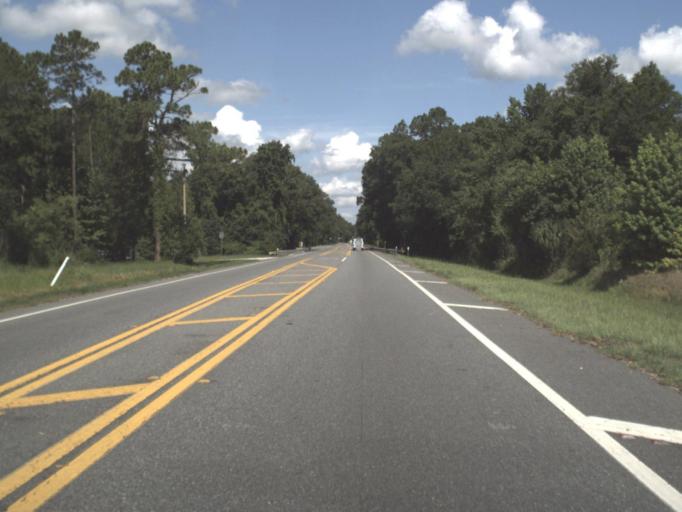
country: US
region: Florida
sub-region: Putnam County
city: Palatka
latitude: 29.6659
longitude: -81.6916
